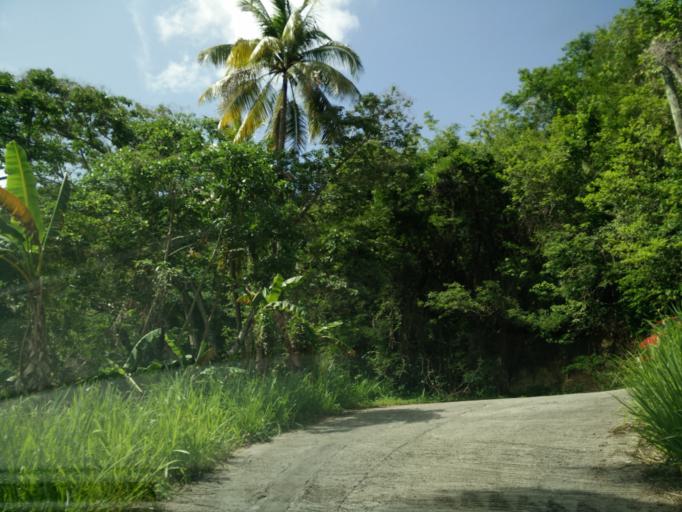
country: MQ
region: Martinique
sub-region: Martinique
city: Saint-Pierre
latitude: 14.7172
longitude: -61.1660
